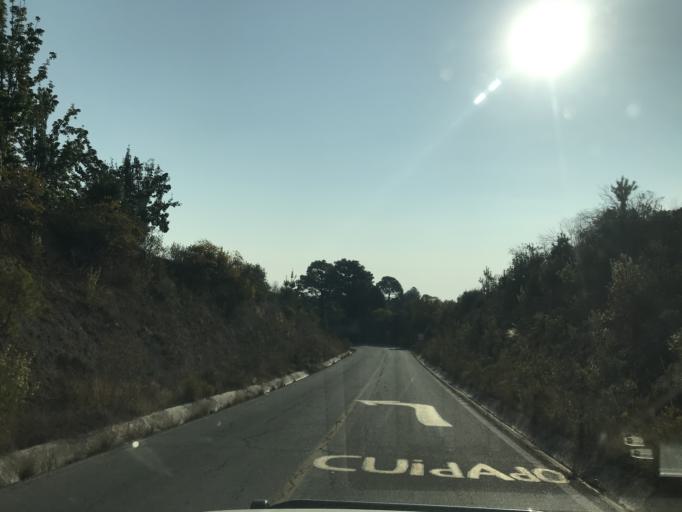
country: MX
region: Puebla
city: San Nicolas de los Ranchos
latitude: 19.0815
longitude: -98.5337
